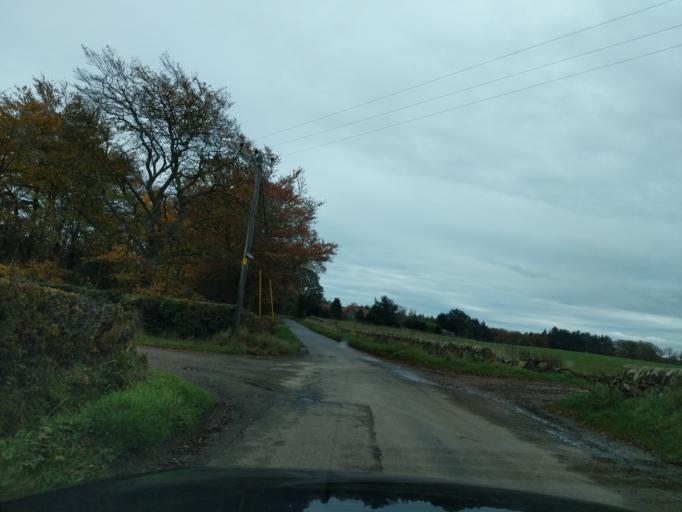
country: GB
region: Scotland
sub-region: Fife
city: Saint Andrews
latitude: 56.2896
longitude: -2.7653
